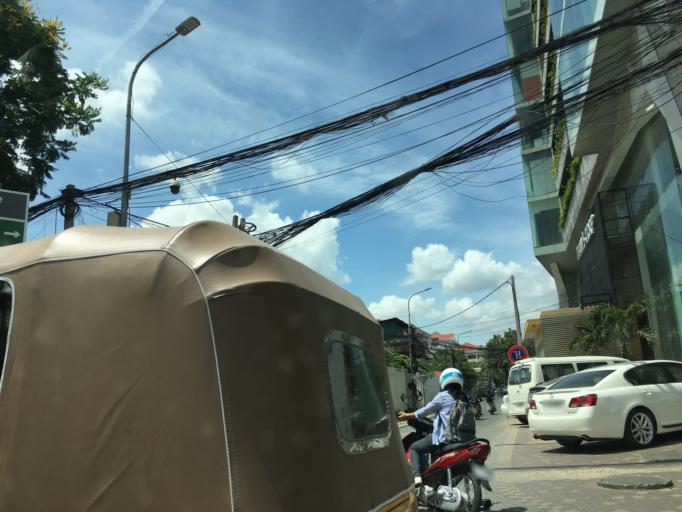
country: KH
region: Phnom Penh
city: Phnom Penh
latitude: 11.5439
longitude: 104.9215
